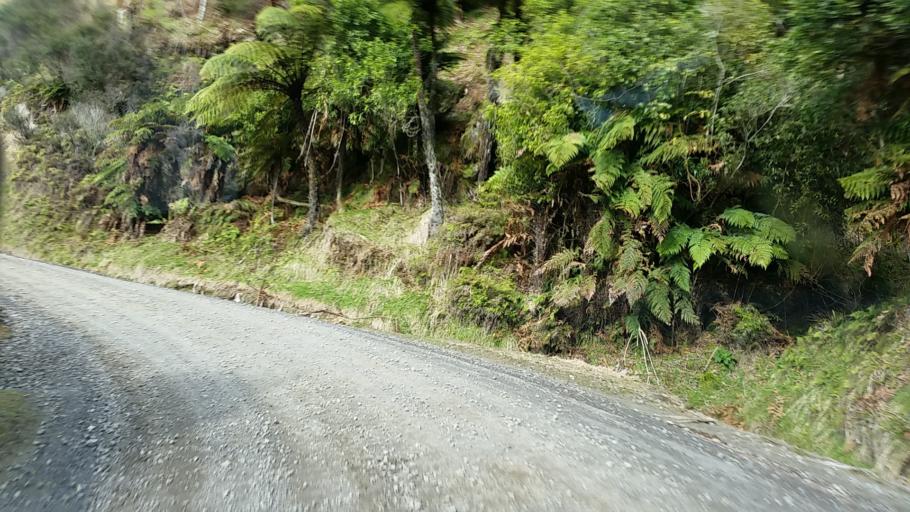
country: NZ
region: Taranaki
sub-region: South Taranaki District
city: Eltham
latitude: -39.1737
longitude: 174.6150
